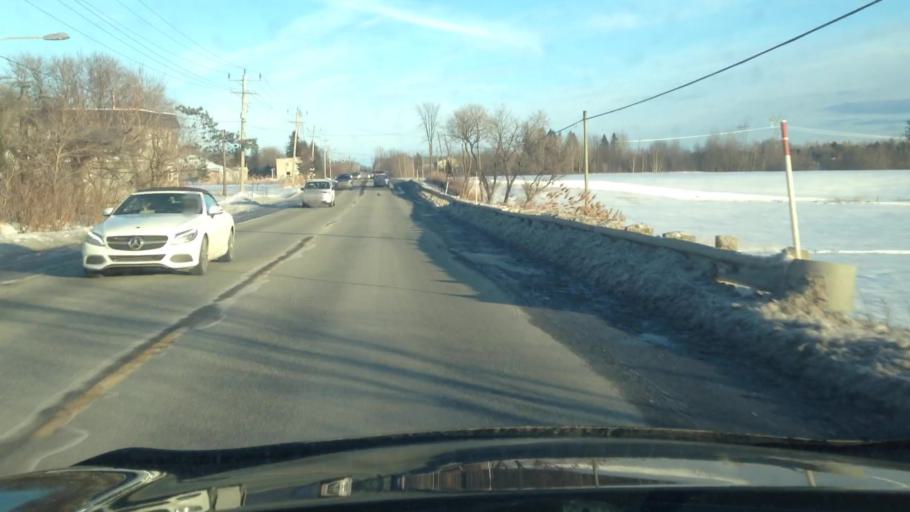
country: CA
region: Quebec
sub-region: Laurentides
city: Sainte-Sophie
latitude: 45.8351
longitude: -73.8561
